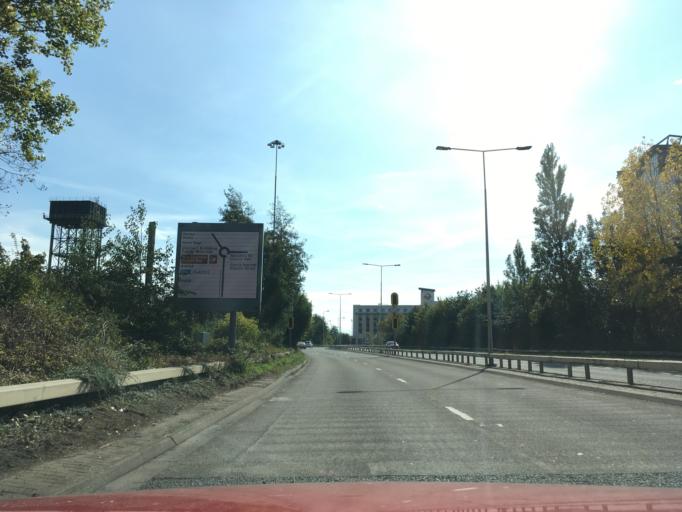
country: GB
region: Wales
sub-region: Cardiff
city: Cardiff
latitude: 51.4707
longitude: -3.1603
